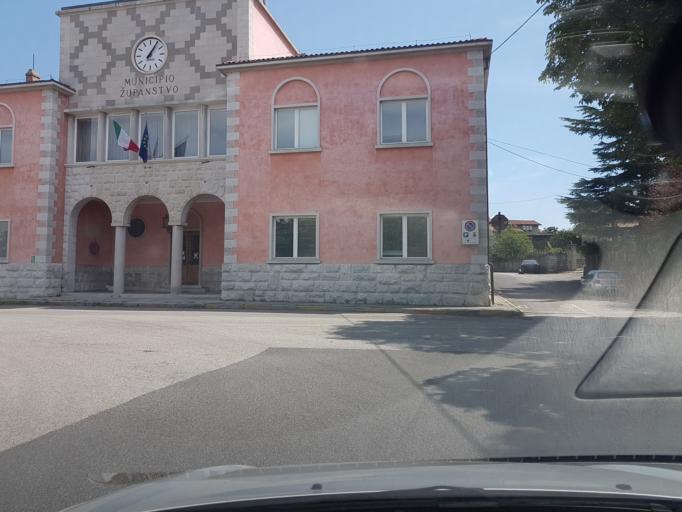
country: IT
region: Friuli Venezia Giulia
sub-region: Provincia di Trieste
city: Aurisina Cave
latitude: 45.7537
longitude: 13.6593
